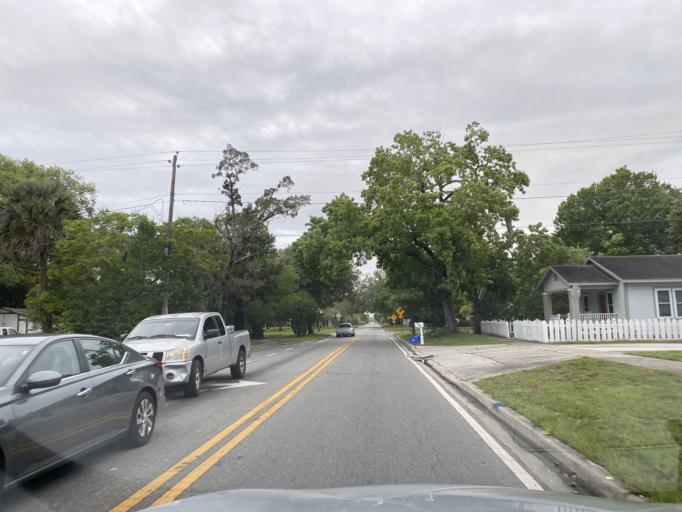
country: US
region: Florida
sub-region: Seminole County
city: Sanford
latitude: 28.8008
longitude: -81.2651
